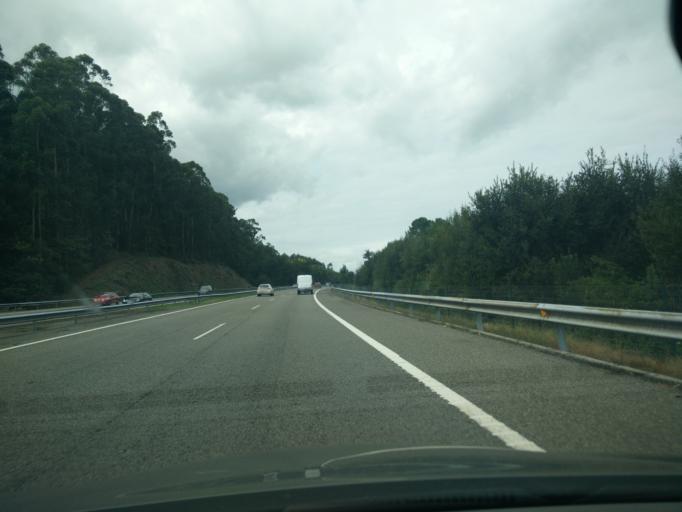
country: ES
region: Galicia
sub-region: Provincia da Coruna
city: Cambre
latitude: 43.3028
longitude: -8.3317
